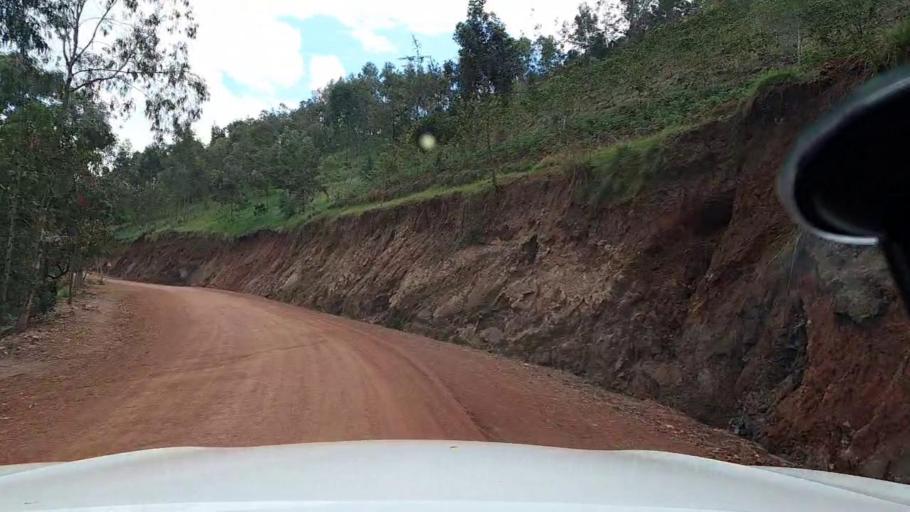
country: RW
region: Northern Province
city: Byumba
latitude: -1.7542
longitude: 29.8459
